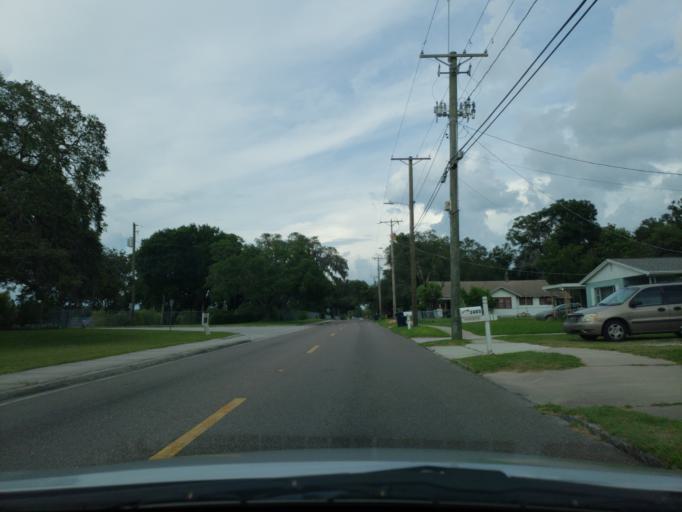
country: US
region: Florida
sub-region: Hillsborough County
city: Tampa
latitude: 27.9888
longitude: -82.4326
